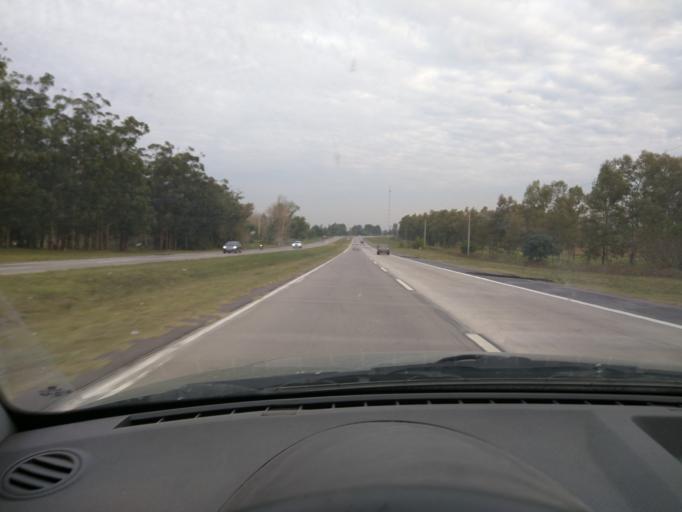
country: AR
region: Buenos Aires
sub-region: Partido de Campana
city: Campana
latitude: -34.2218
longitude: -58.9590
